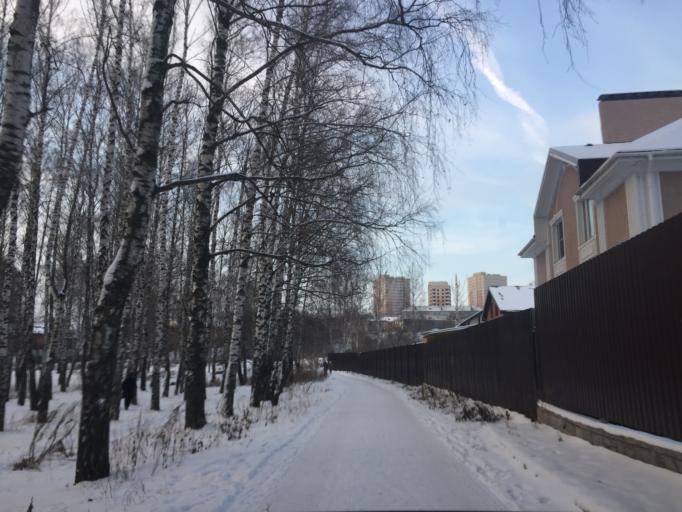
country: RU
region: Tula
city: Tula
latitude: 54.2016
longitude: 37.6656
